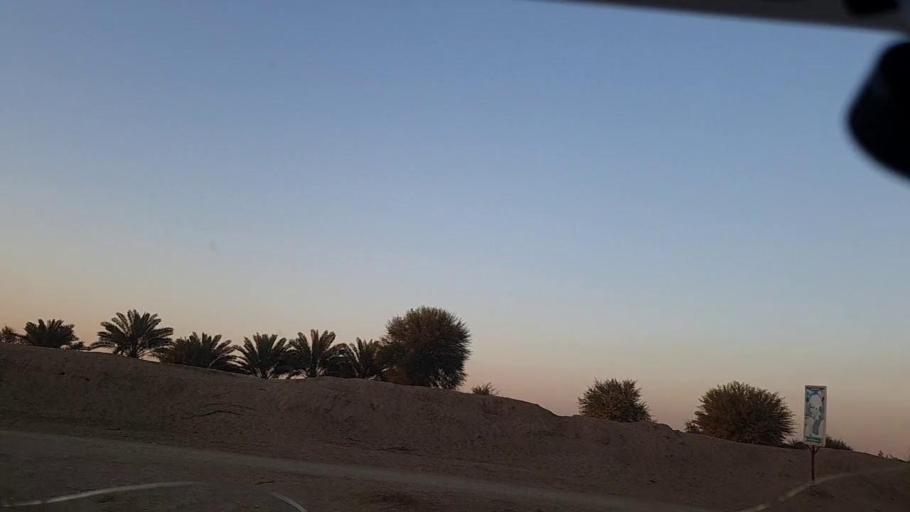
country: PK
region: Sindh
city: Adilpur
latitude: 27.8442
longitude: 69.2967
